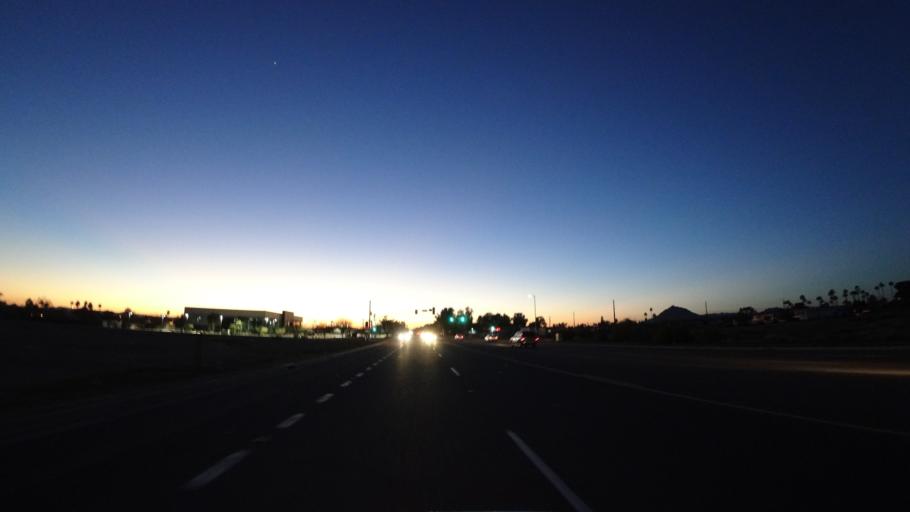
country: US
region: Arizona
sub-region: Maricopa County
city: Scottsdale
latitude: 33.4658
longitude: -111.8910
